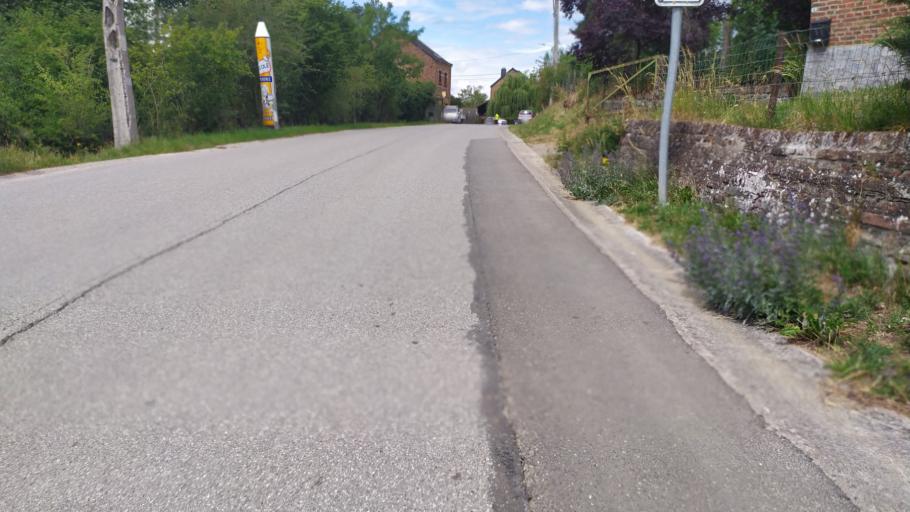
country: BE
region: Wallonia
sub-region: Province de Namur
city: Houyet
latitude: 50.1614
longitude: 5.0402
